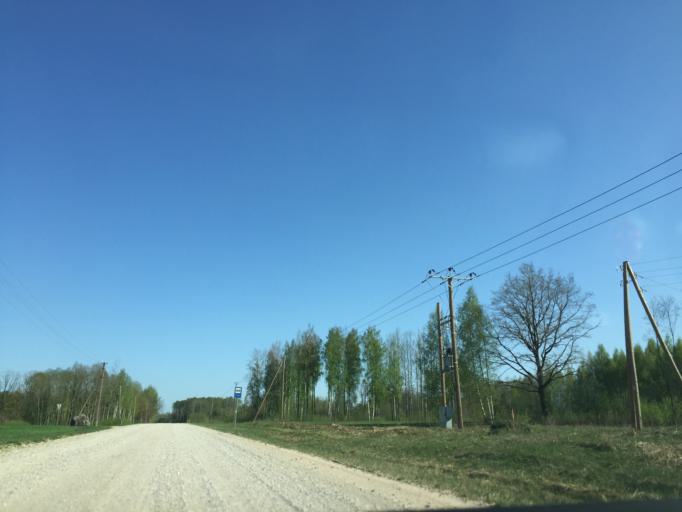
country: LV
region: Skriveri
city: Skriveri
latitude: 56.8416
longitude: 25.0975
